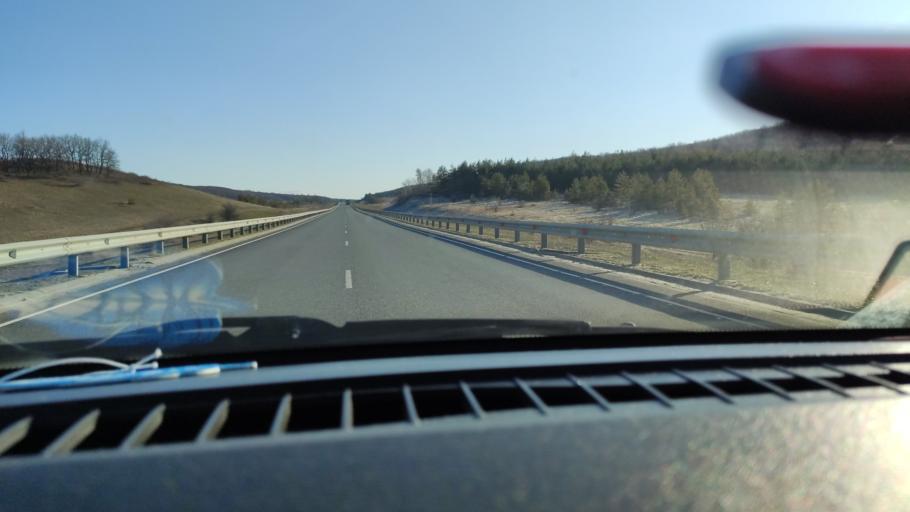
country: RU
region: Saratov
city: Alekseyevka
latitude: 52.4012
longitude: 47.9911
